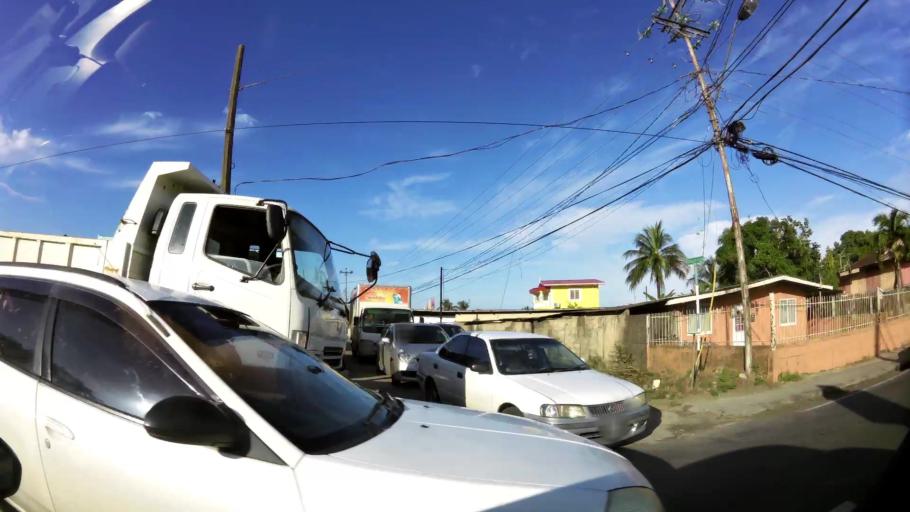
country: TT
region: Tunapuna/Piarco
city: Arouca
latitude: 10.5862
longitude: -61.3385
